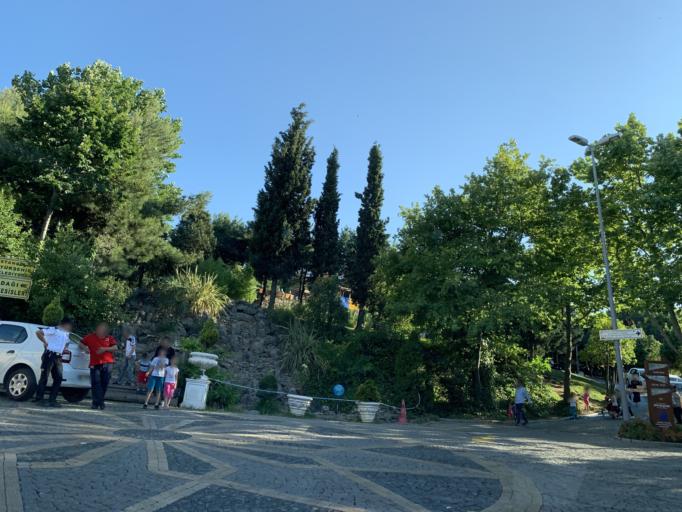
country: TR
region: Istanbul
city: Pendik
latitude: 40.8928
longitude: 29.2538
